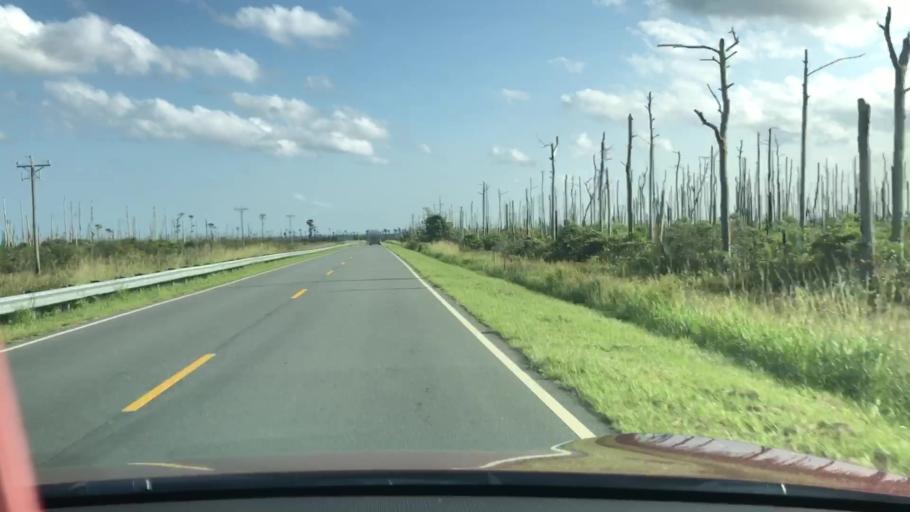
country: US
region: North Carolina
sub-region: Dare County
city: Wanchese
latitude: 35.6499
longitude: -75.7776
